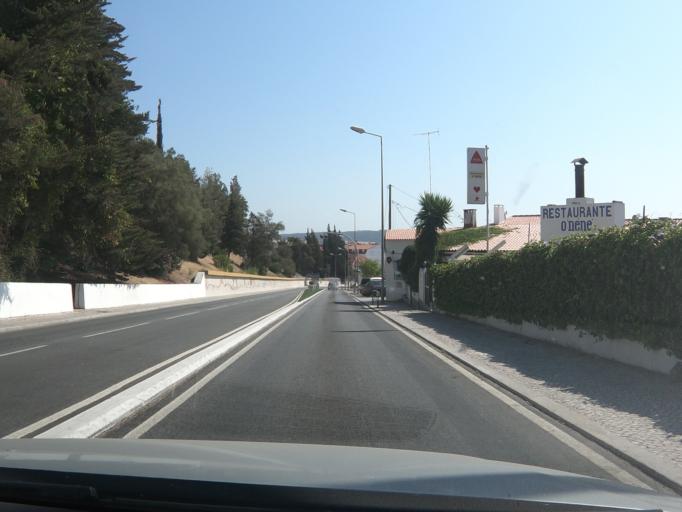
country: PT
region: Setubal
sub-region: Alcacer do Sal
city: Alcacer do Sal
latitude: 38.3724
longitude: -8.5076
